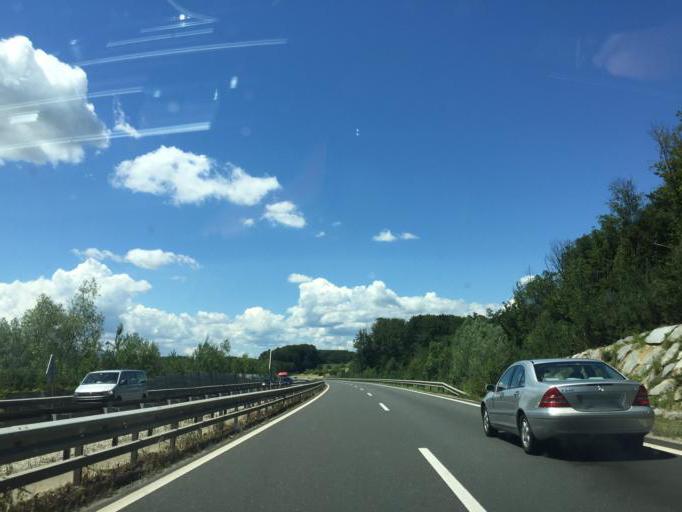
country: SI
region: Lenart
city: Lenart v Slov. Goricah
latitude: 46.5774
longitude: 15.8041
